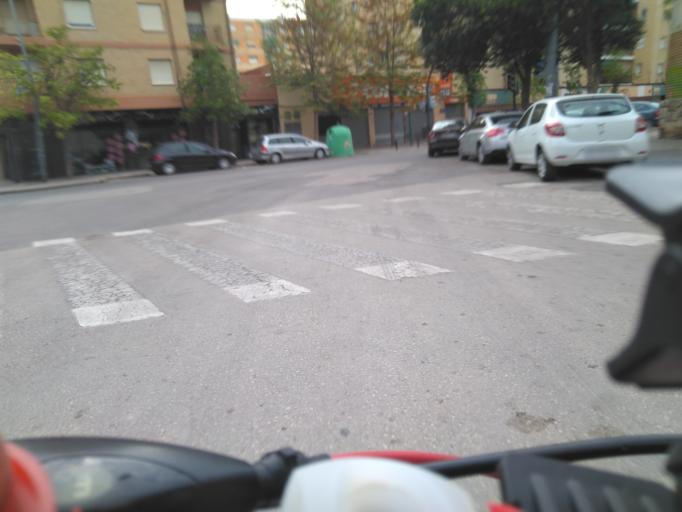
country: ES
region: Valencia
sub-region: Provincia de Valencia
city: Tavernes Blanques
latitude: 39.4915
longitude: -0.3861
